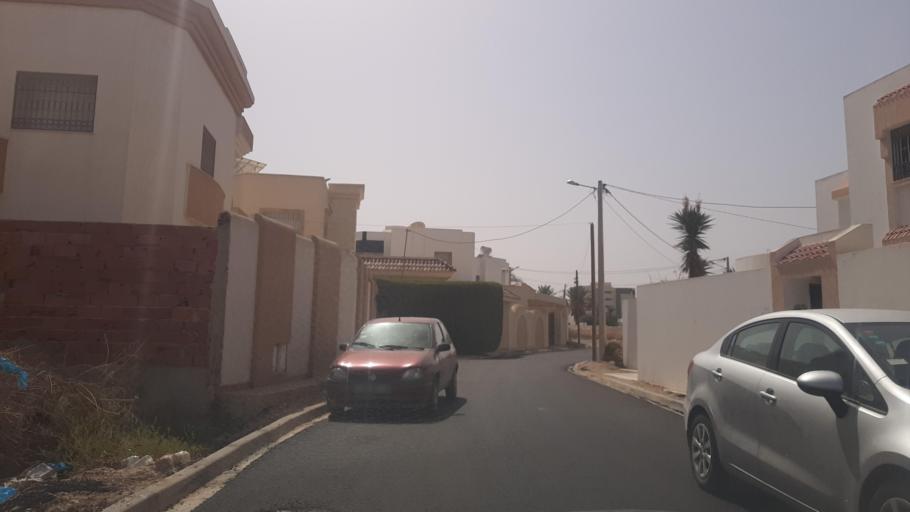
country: TN
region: Safaqis
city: Sfax
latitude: 34.7597
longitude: 10.7593
